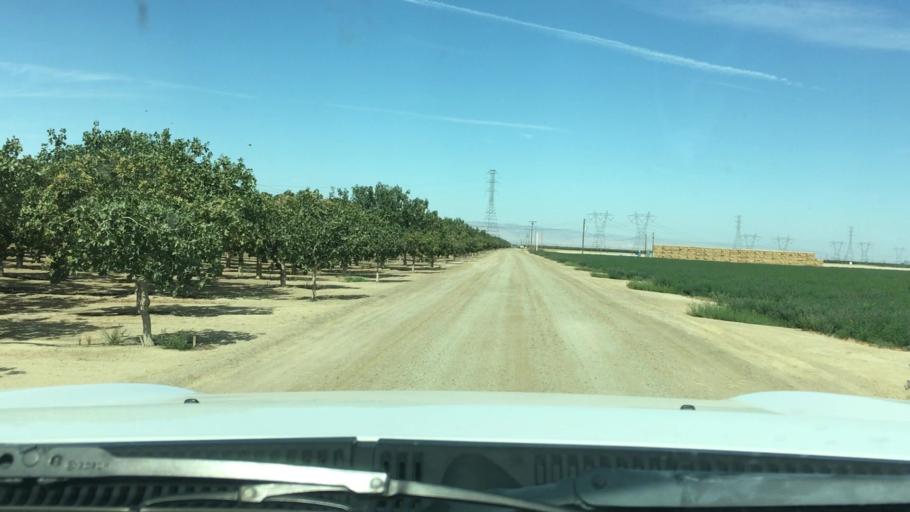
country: US
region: California
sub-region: Kern County
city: Buttonwillow
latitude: 35.3766
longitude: -119.3916
